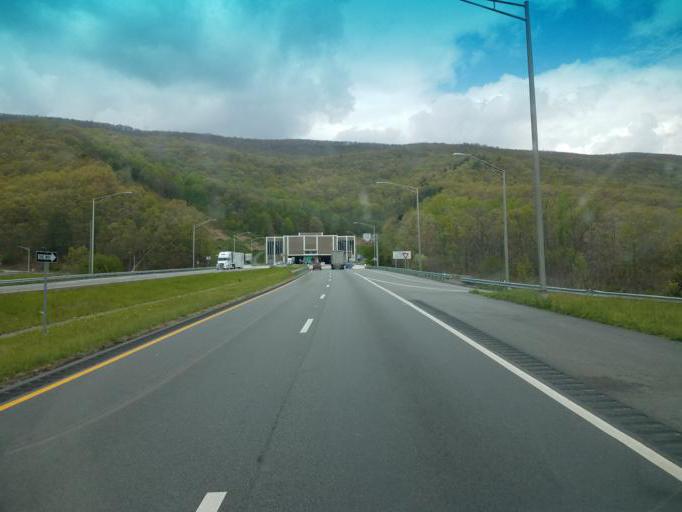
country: US
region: West Virginia
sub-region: Mercer County
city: Bluefield
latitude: 37.2637
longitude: -81.1211
